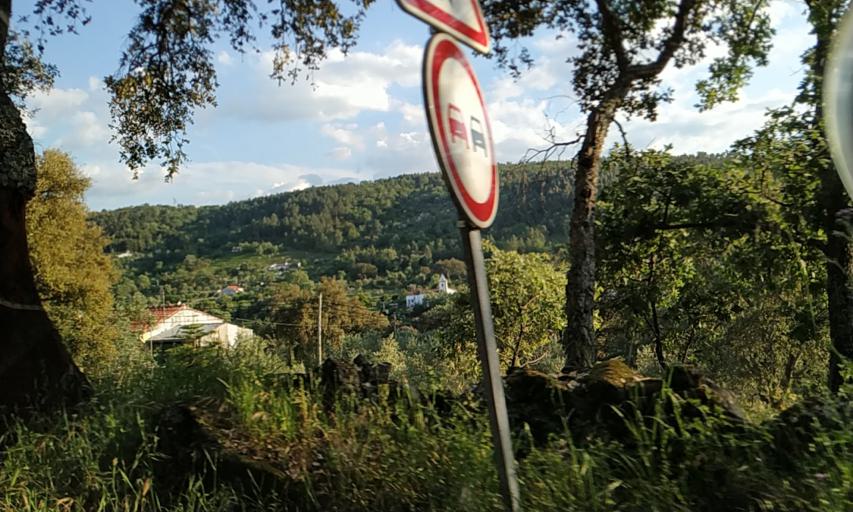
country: PT
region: Portalegre
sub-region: Portalegre
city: Portalegre
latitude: 39.3264
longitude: -7.4232
